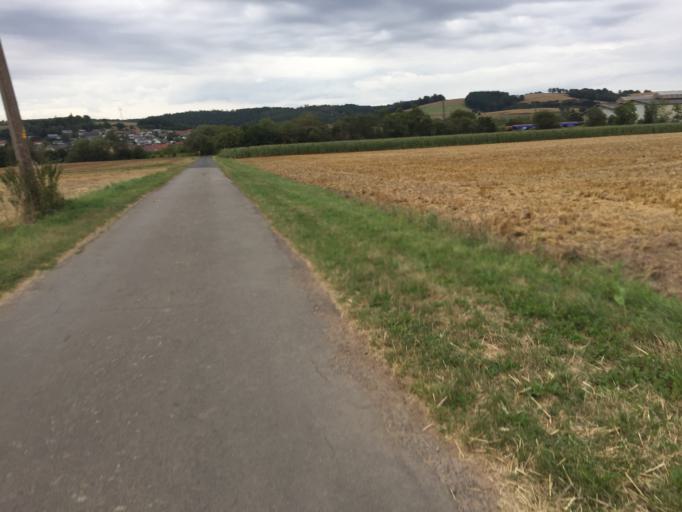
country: DE
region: Hesse
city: Bebra
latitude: 50.9850
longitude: 9.7706
